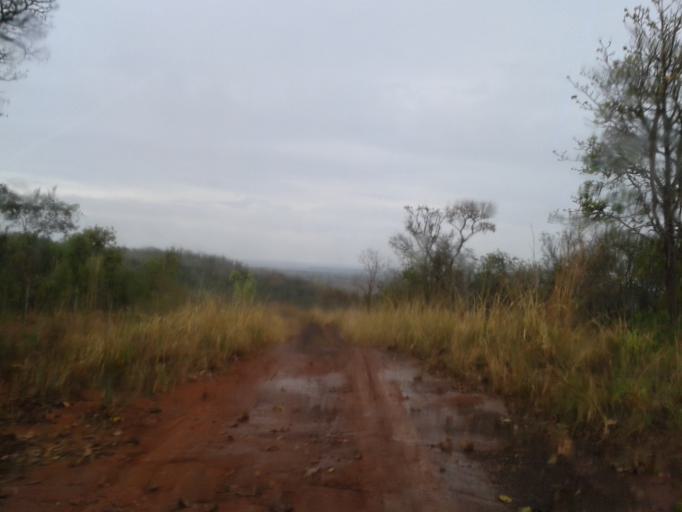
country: BR
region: Minas Gerais
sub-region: Campina Verde
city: Campina Verde
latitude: -19.3337
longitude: -49.5184
